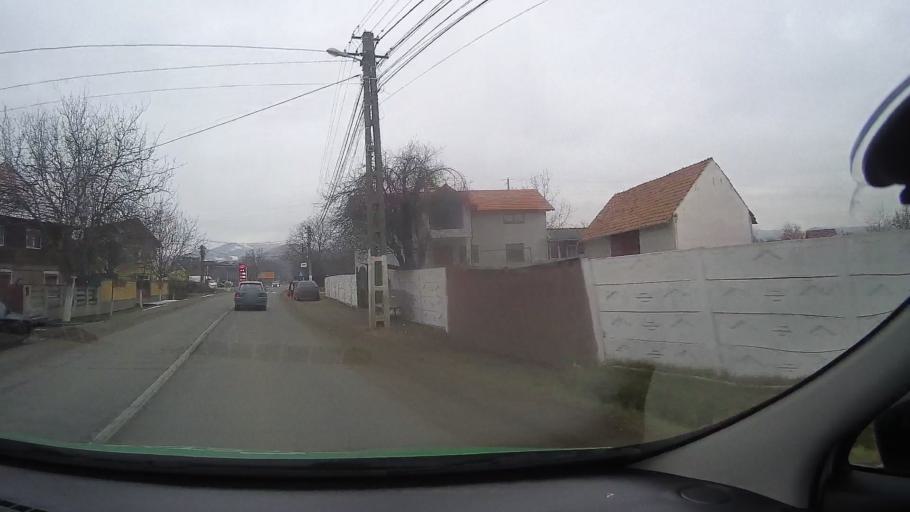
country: RO
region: Alba
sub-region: Comuna Ighiu
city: Sard
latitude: 46.1212
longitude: 23.5272
